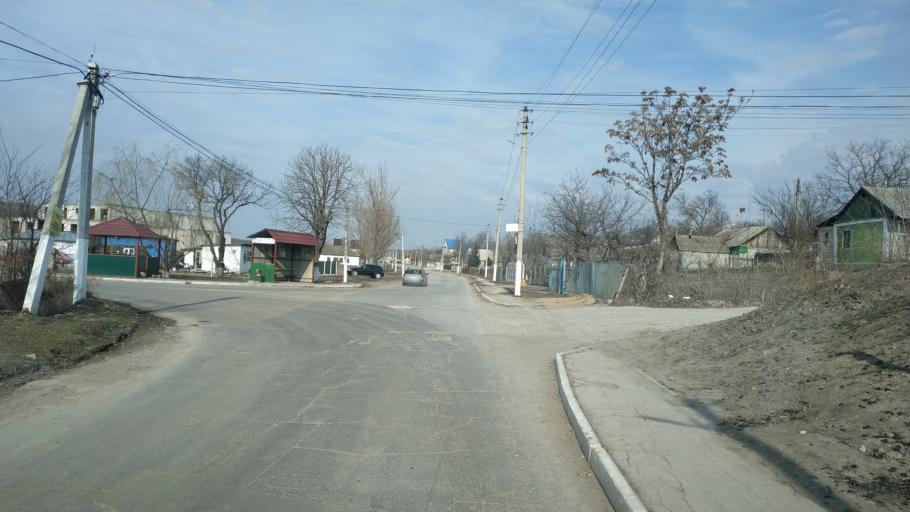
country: MD
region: Anenii Noi
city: Anenii Noi
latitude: 46.9207
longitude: 29.1076
